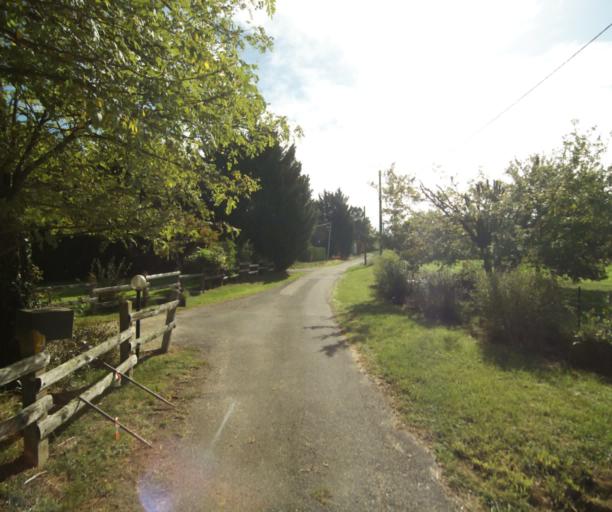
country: FR
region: Midi-Pyrenees
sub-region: Departement du Gers
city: Cazaubon
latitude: 43.8488
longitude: -0.0671
